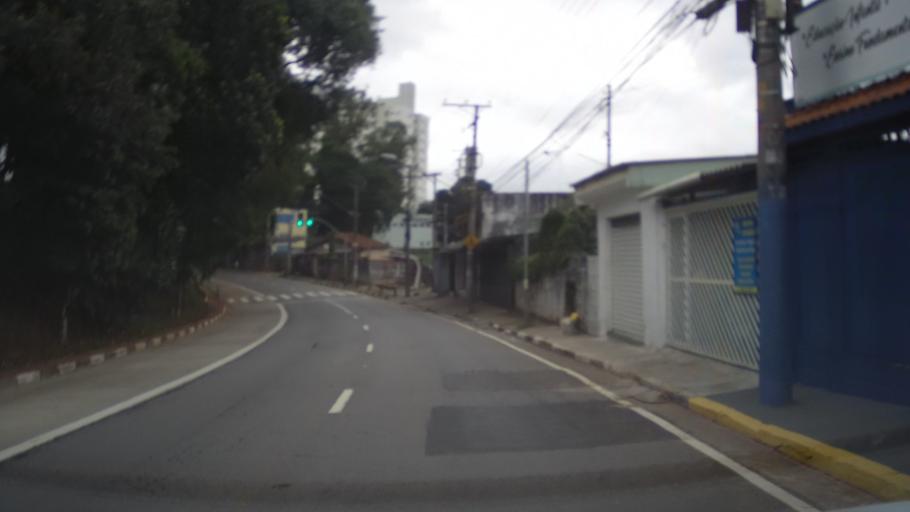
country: BR
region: Sao Paulo
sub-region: Guarulhos
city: Guarulhos
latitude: -23.4629
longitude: -46.5480
